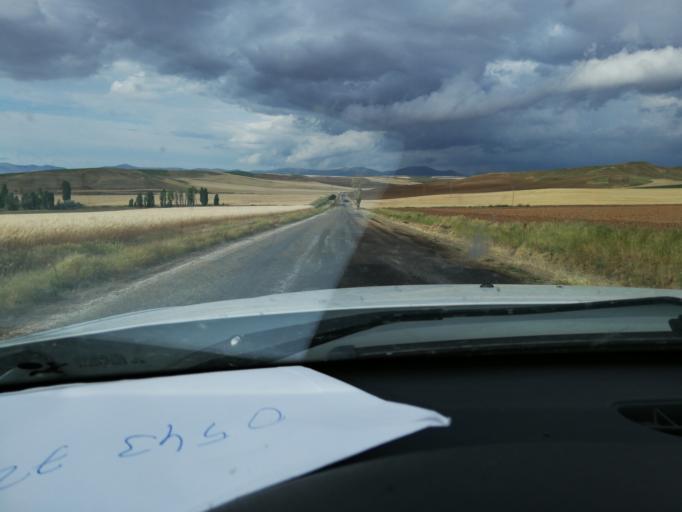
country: TR
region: Kirsehir
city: Kirsehir
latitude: 39.0353
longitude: 34.1436
